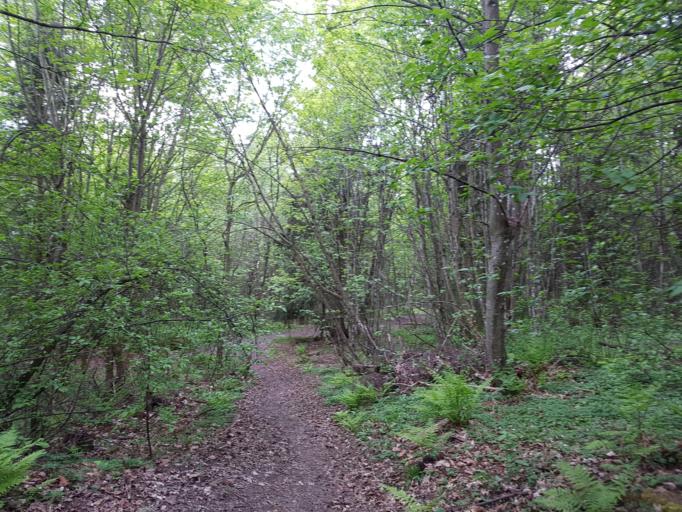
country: NO
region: Nord-Trondelag
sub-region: Levanger
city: Levanger
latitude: 63.7406
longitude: 11.2639
